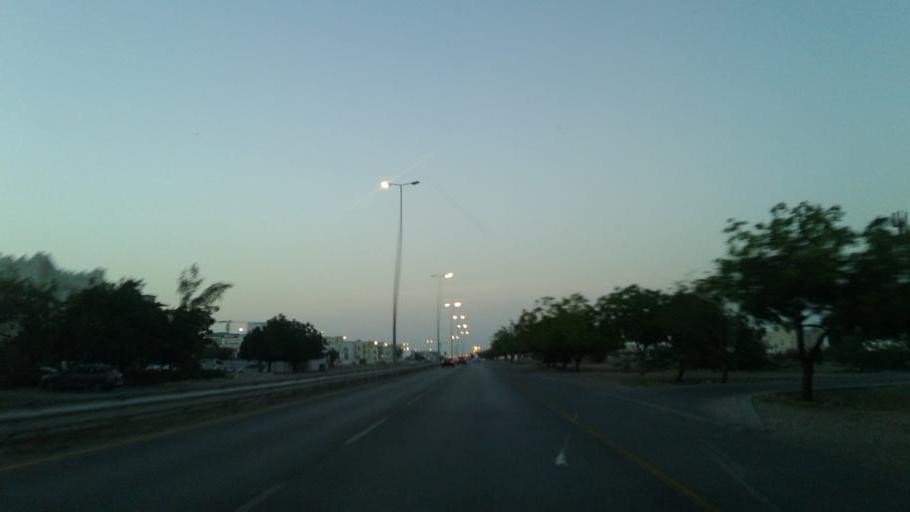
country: OM
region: Muhafazat Masqat
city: As Sib al Jadidah
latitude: 23.6073
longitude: 58.2168
